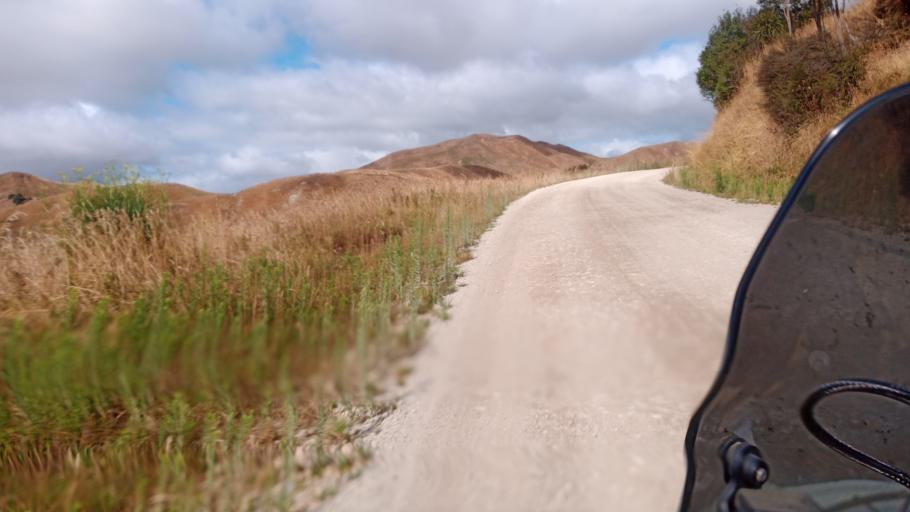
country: NZ
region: Hawke's Bay
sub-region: Wairoa District
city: Wairoa
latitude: -38.6087
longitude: 177.4627
